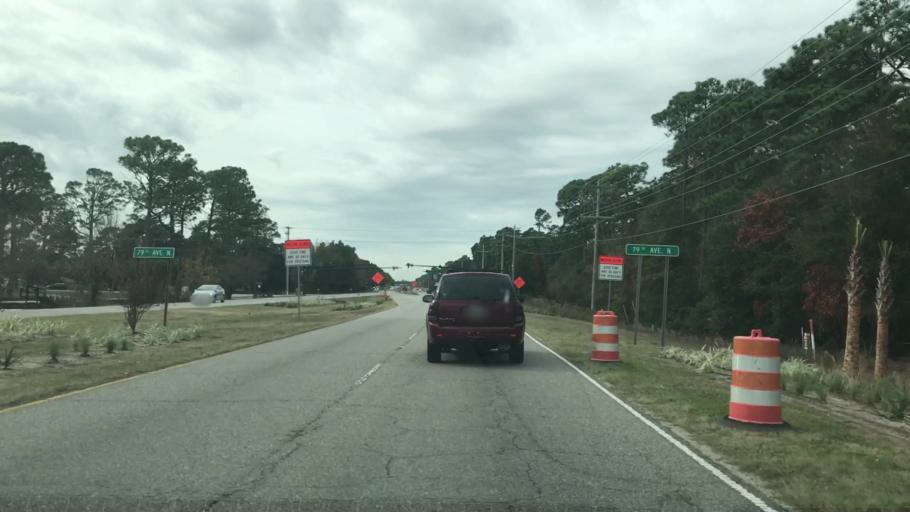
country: US
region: South Carolina
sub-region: Horry County
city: Myrtle Beach
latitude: 33.7578
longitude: -78.8235
